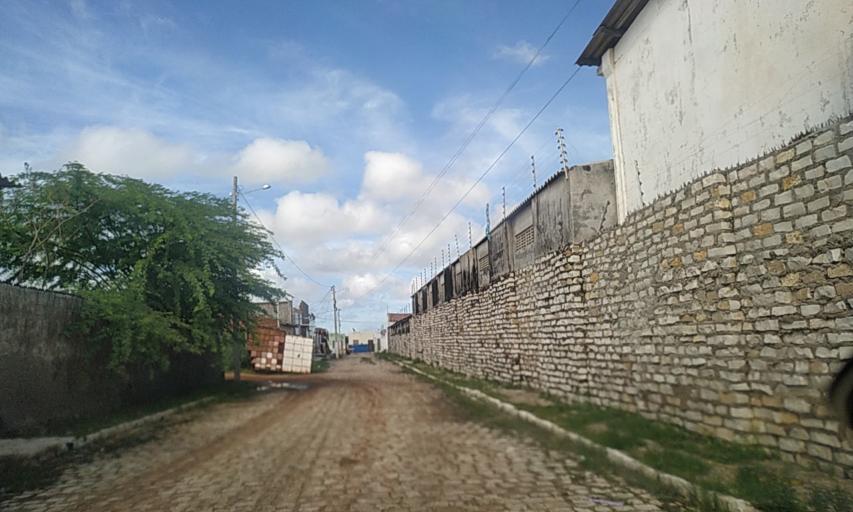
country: BR
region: Rio Grande do Norte
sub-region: Areia Branca
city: Areia Branca
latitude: -4.9544
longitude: -37.1282
